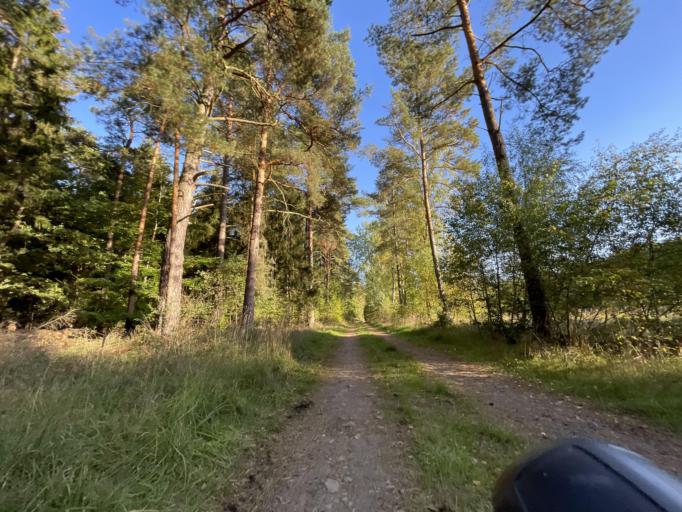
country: DE
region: Lower Saxony
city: Vastorf
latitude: 53.1986
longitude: 10.5198
